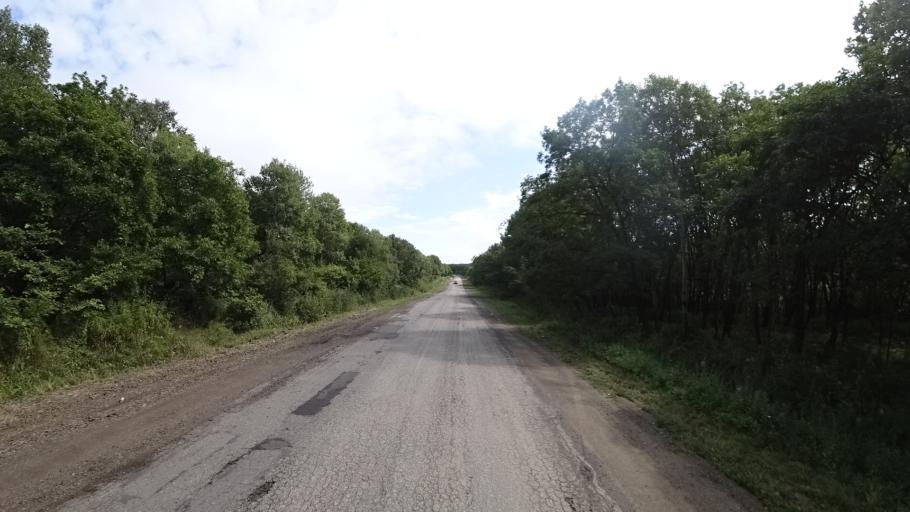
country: RU
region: Primorskiy
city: Lyalichi
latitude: 44.1469
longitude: 132.3989
